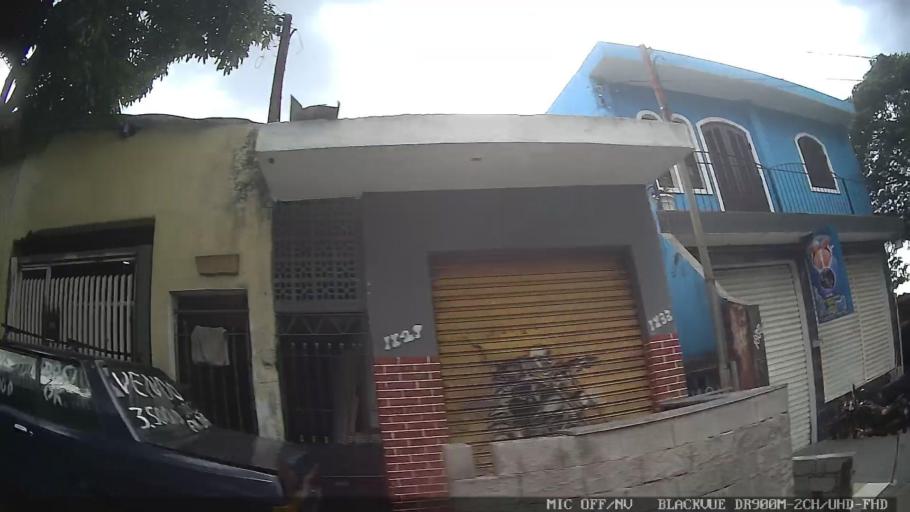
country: BR
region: Sao Paulo
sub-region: Ferraz De Vasconcelos
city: Ferraz de Vasconcelos
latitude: -23.5538
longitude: -46.3607
